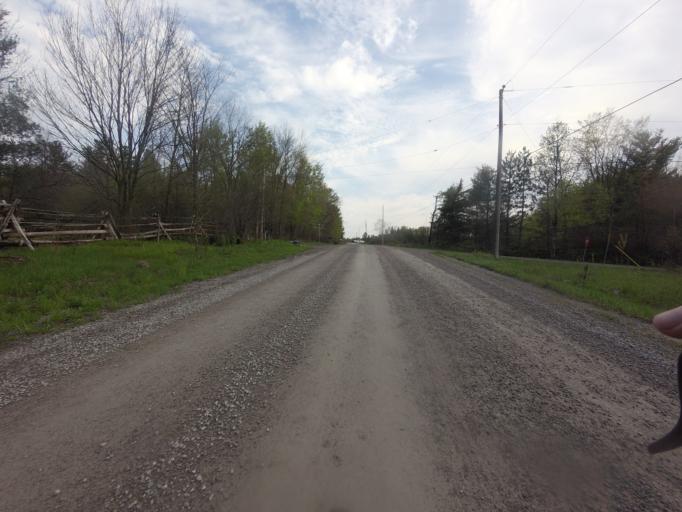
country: CA
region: Ontario
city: Carleton Place
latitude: 45.2041
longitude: -76.3224
